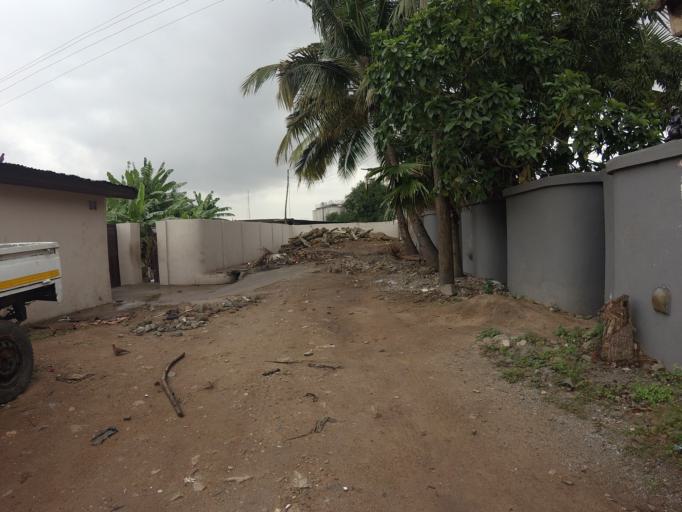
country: GH
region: Greater Accra
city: Dome
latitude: 5.6336
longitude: -0.2342
